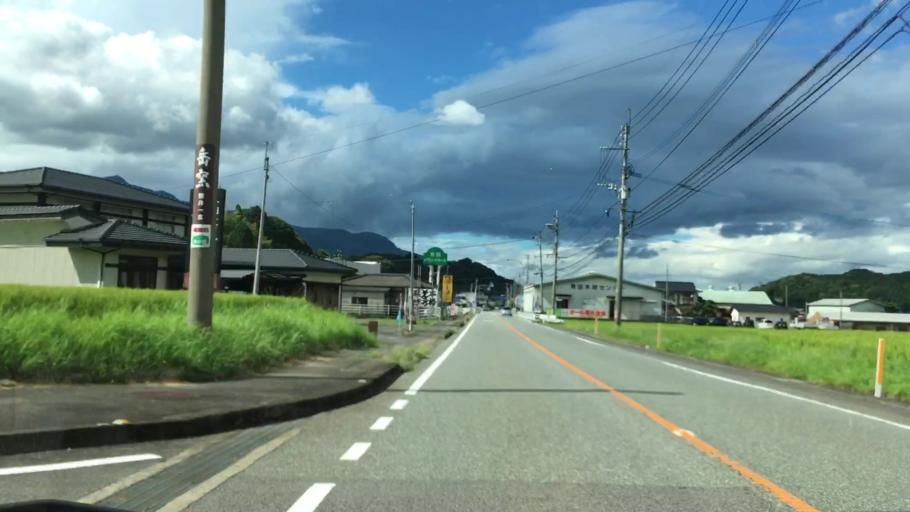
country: JP
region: Saga Prefecture
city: Imaricho-ko
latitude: 33.1900
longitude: 129.8519
